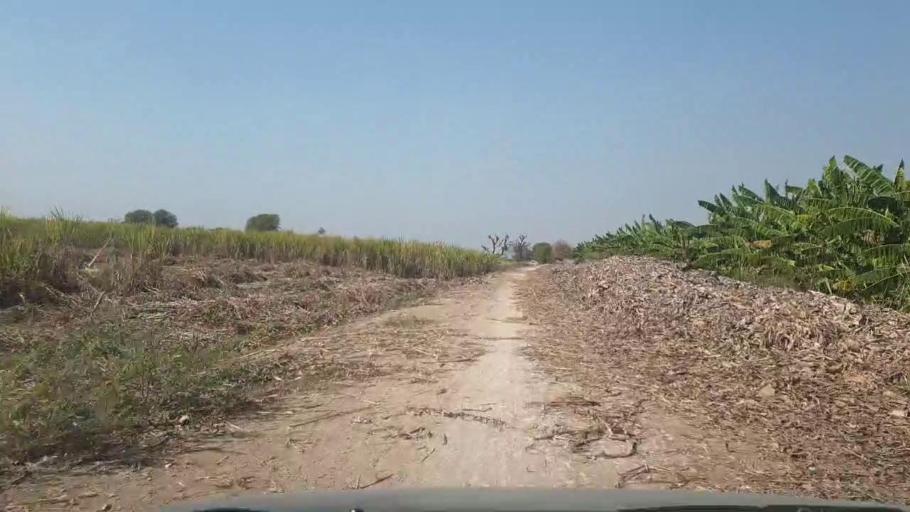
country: PK
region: Sindh
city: Chambar
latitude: 25.3277
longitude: 68.8662
